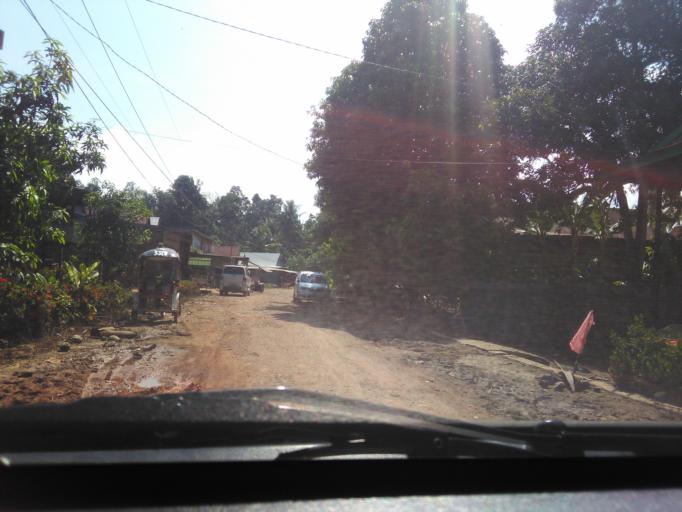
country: ID
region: South Sulawesi
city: Tancung
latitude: -4.0155
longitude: 119.9250
